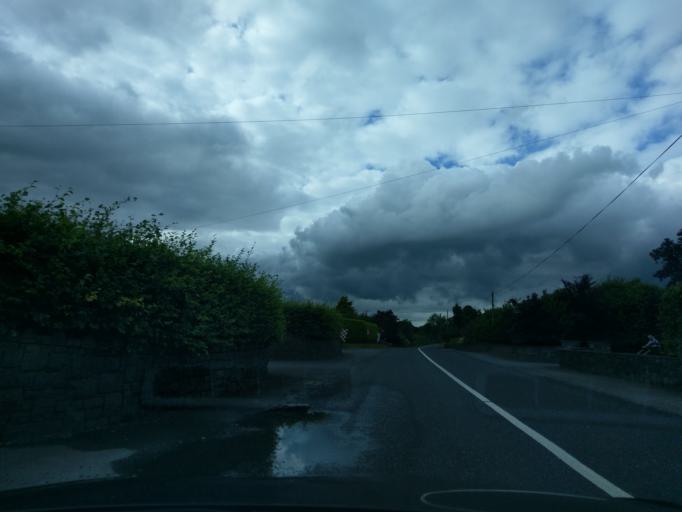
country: IE
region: Connaught
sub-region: County Galway
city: Athenry
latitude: 53.2609
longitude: -8.7401
